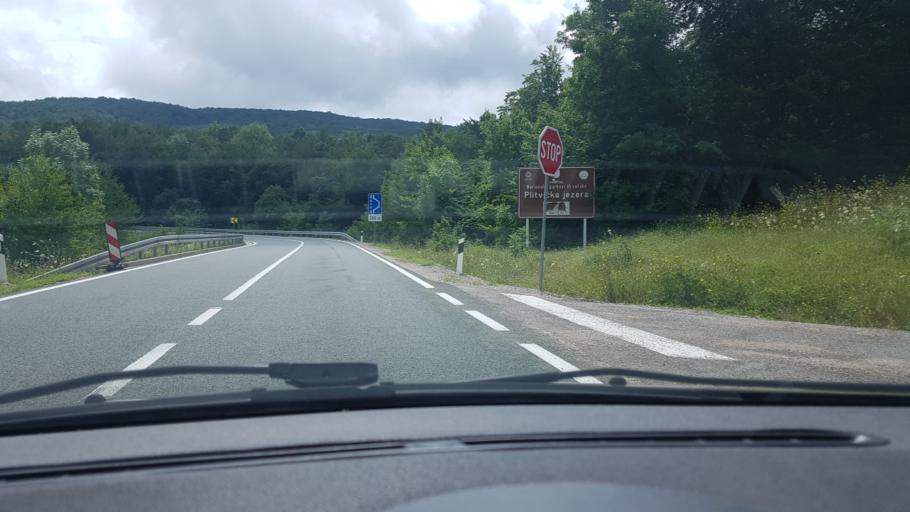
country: HR
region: Licko-Senjska
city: Jezerce
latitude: 44.8853
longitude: 15.6927
